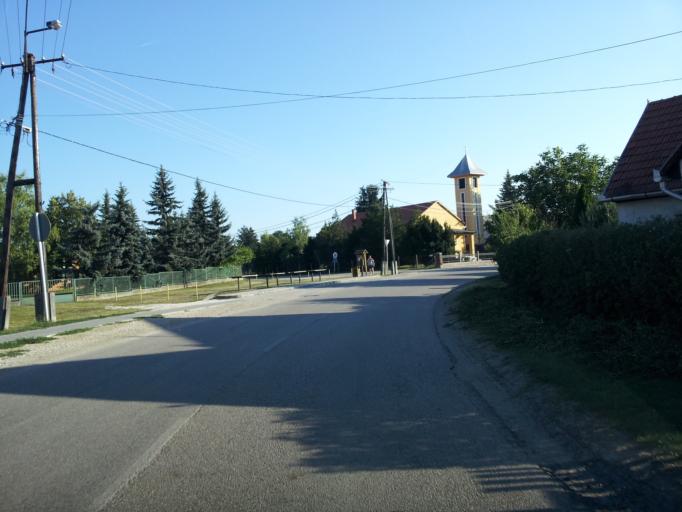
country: HU
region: Fejer
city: Lepseny
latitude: 47.0190
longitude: 18.2103
